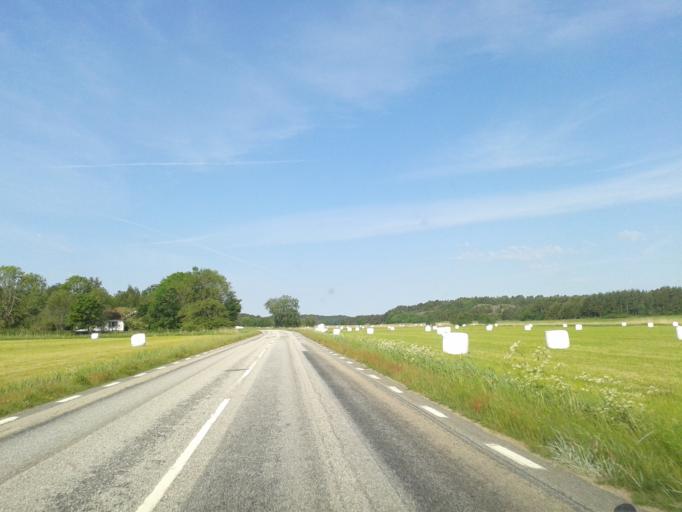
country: SE
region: Vaestra Goetaland
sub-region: Stromstads Kommun
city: Stroemstad
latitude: 58.8615
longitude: 11.2491
